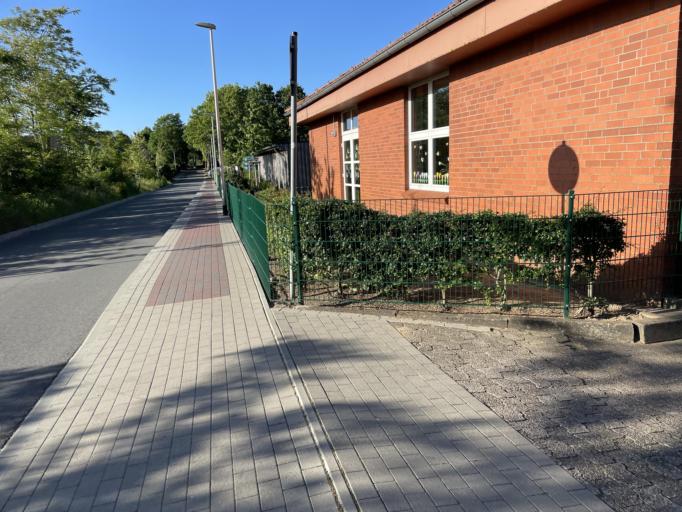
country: DE
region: Schleswig-Holstein
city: Mildstedt
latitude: 54.4605
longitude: 9.0978
